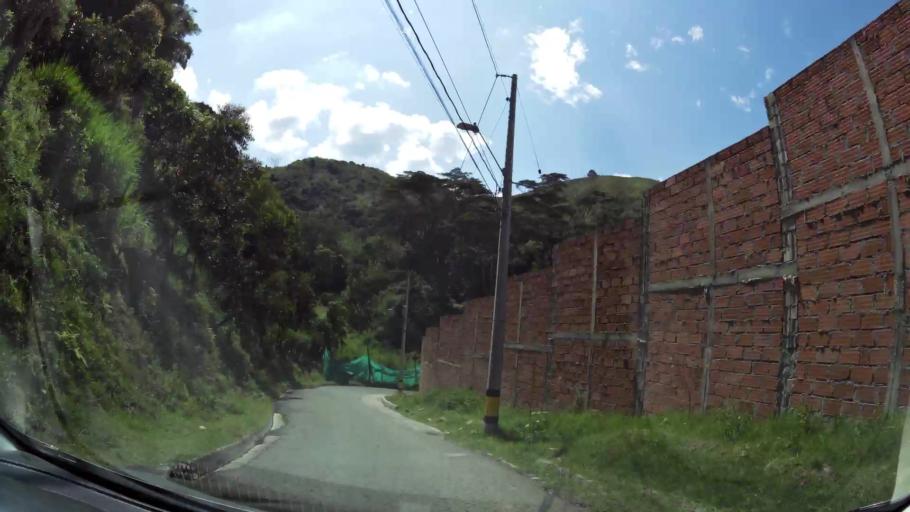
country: CO
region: Antioquia
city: Itagui
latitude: 6.2098
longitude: -75.6101
